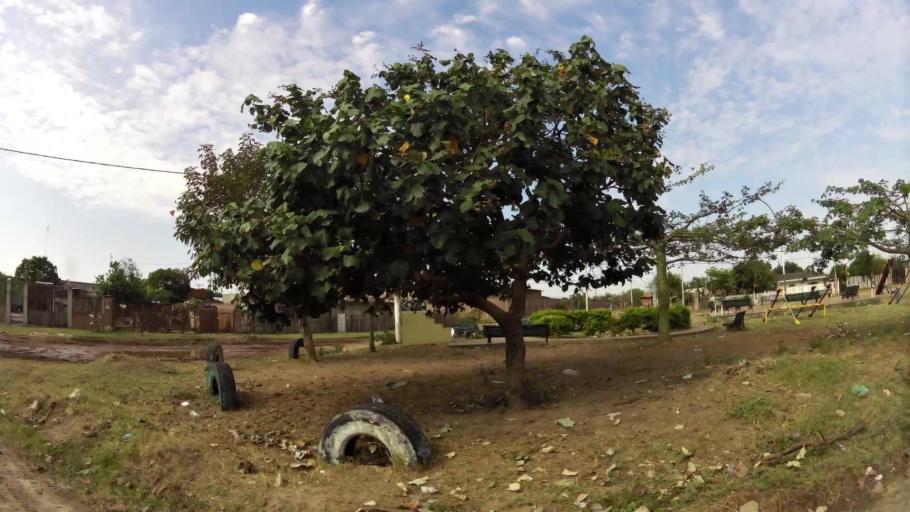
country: BO
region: Santa Cruz
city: Santa Cruz de la Sierra
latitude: -17.7368
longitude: -63.1379
